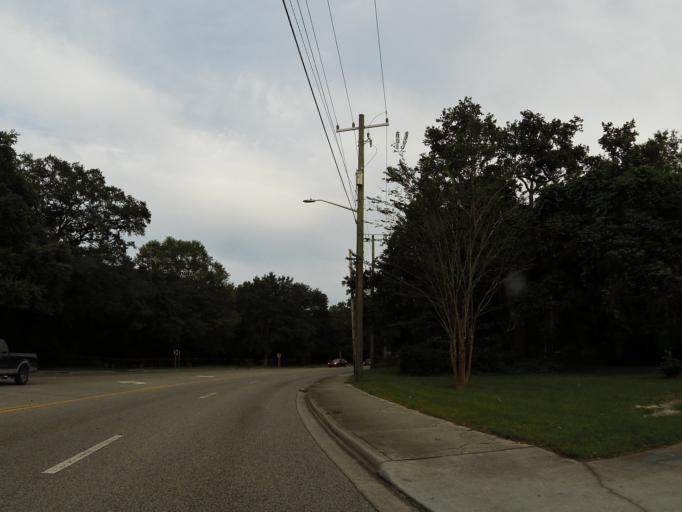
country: US
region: Florida
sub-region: Duval County
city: Jacksonville
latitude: 30.3822
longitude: -81.6979
